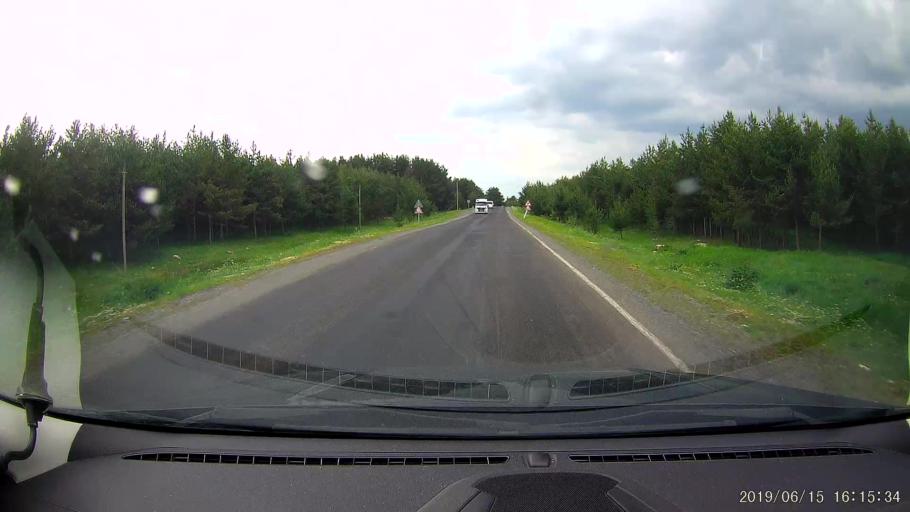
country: TR
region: Ardahan
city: Hanak
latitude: 41.2669
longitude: 42.8564
